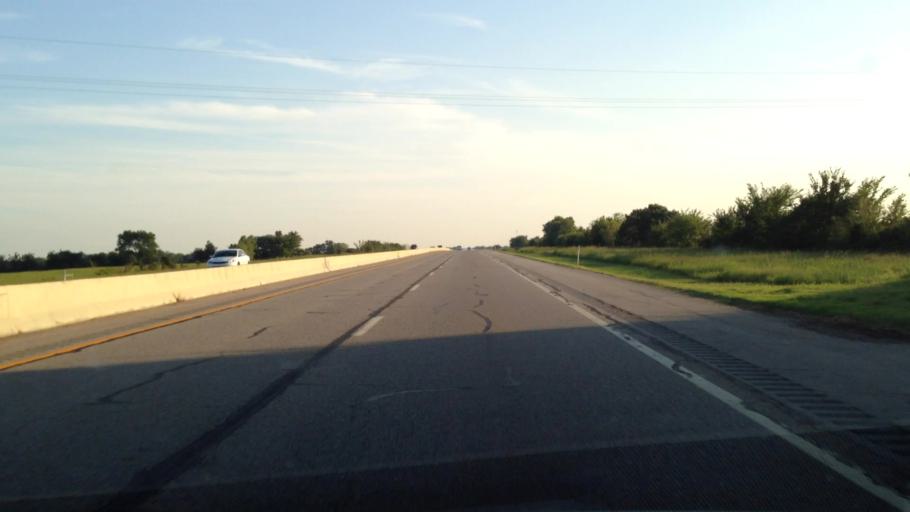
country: US
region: Oklahoma
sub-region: Ottawa County
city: Fairland
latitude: 36.8010
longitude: -94.8804
